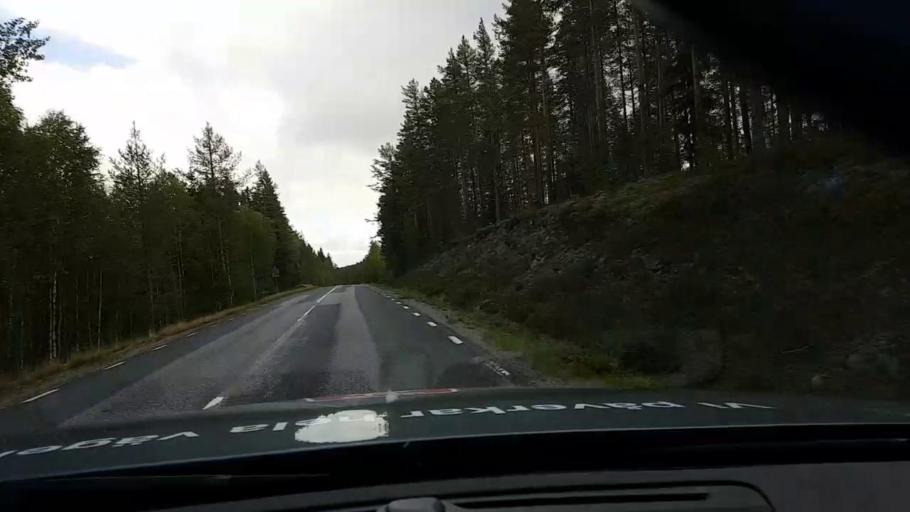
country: SE
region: Vaesterbotten
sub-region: Asele Kommun
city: Asele
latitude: 63.8420
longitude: 17.4258
